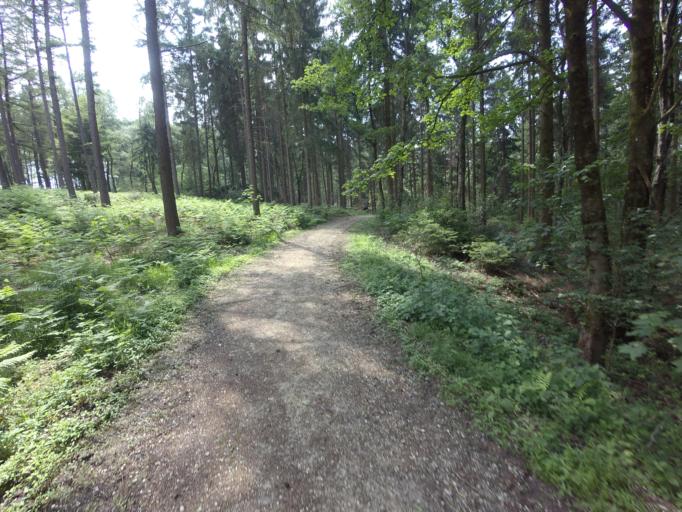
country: BE
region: Wallonia
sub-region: Province de Liege
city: Plombieres
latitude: 50.7814
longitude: 5.9489
